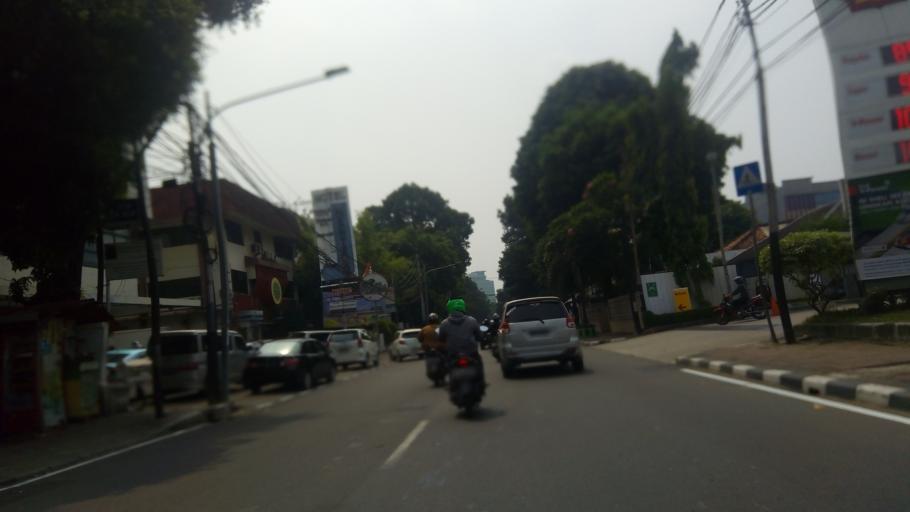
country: ID
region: Jakarta Raya
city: Jakarta
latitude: -6.1909
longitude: 106.8362
